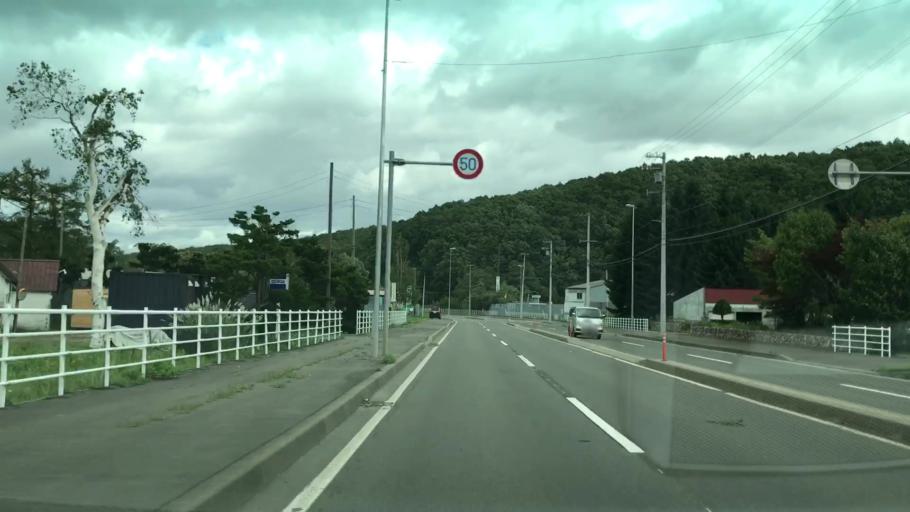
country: JP
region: Hokkaido
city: Kitahiroshima
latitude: 42.9655
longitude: 141.4547
